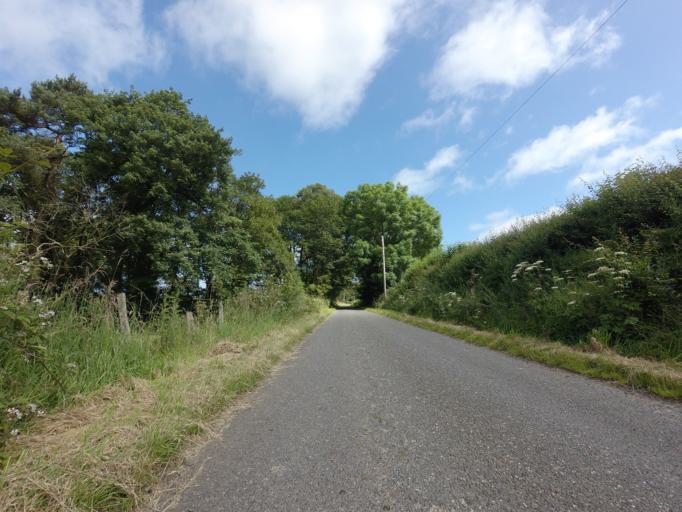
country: GB
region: Scotland
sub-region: Aberdeenshire
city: Turriff
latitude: 57.5829
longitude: -2.5066
